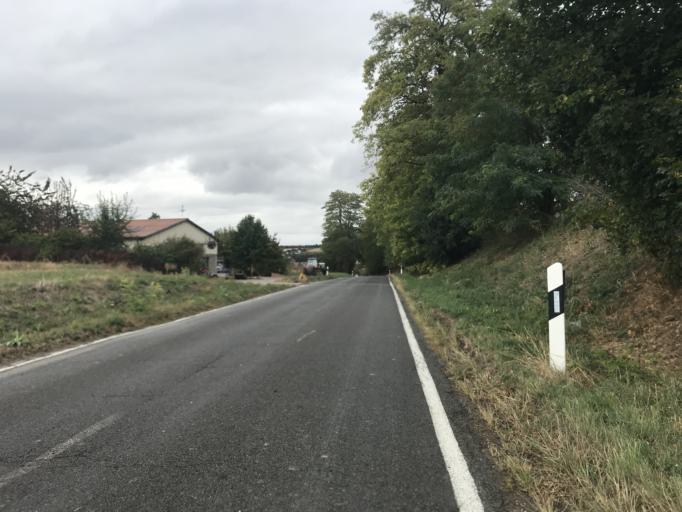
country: DE
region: Rheinland-Pfalz
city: Ober-Saulheim
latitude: 49.8826
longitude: 8.1398
